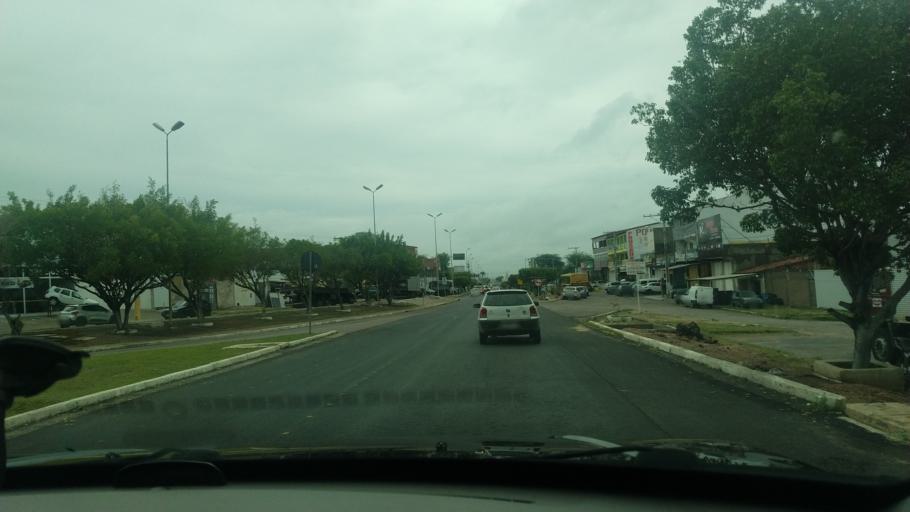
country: BR
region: Bahia
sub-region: Paulo Afonso
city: Paulo Afonso
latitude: -9.4031
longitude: -38.2386
